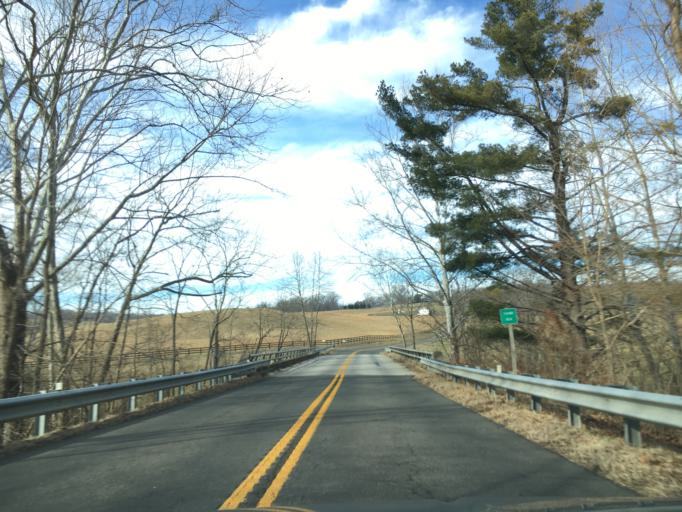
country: US
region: Virginia
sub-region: Fauquier County
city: Marshall
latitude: 38.7658
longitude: -77.9765
